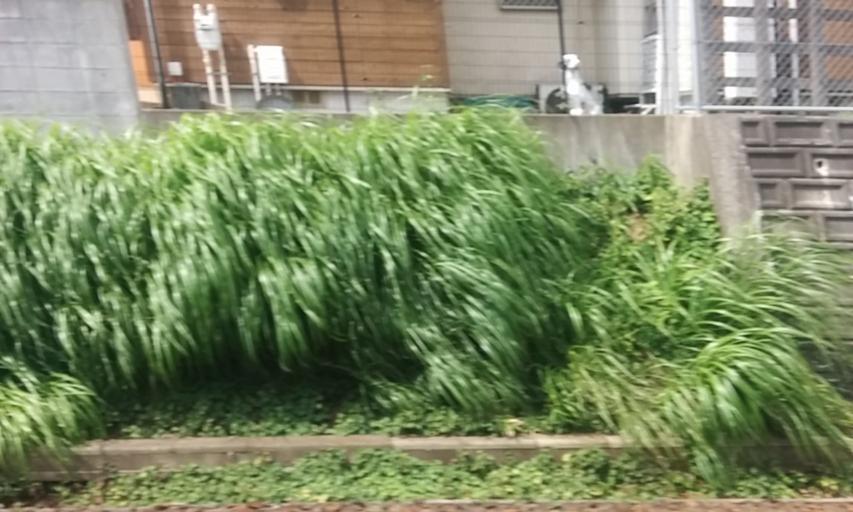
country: JP
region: Chiba
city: Funabashi
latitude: 35.7089
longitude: 139.9671
